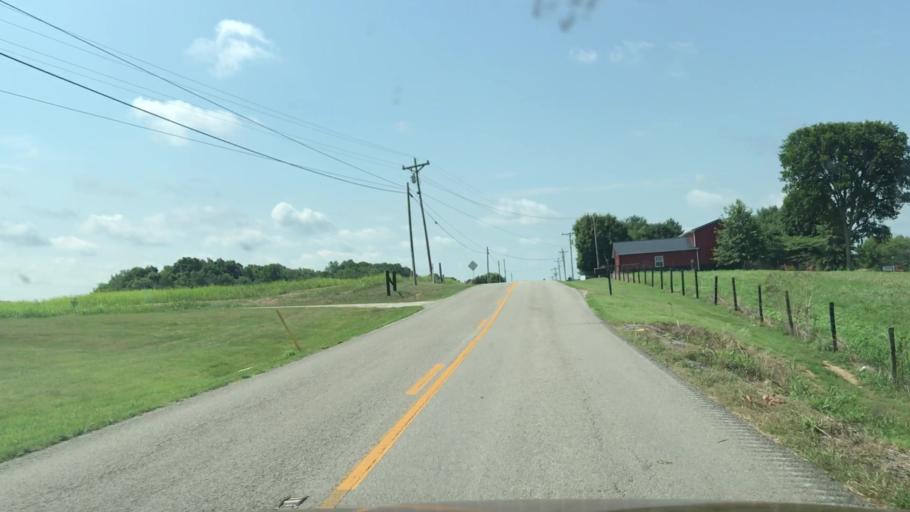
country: US
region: Kentucky
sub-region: Barren County
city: Glasgow
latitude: 36.8764
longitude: -85.8482
